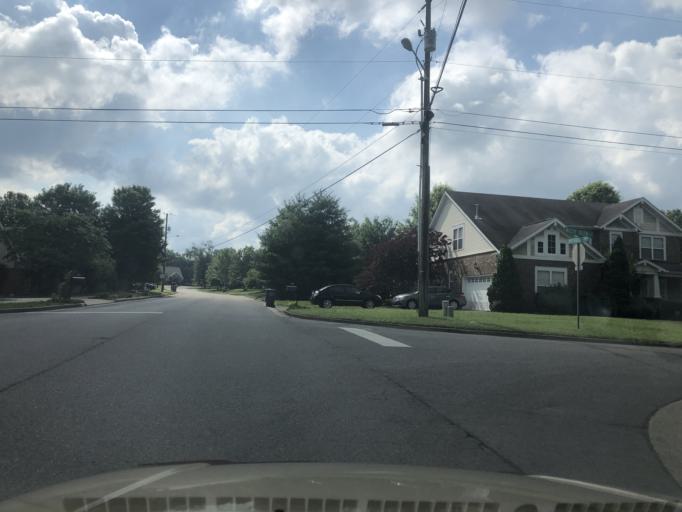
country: US
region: Tennessee
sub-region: Davidson County
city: Lakewood
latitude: 36.2266
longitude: -86.5956
